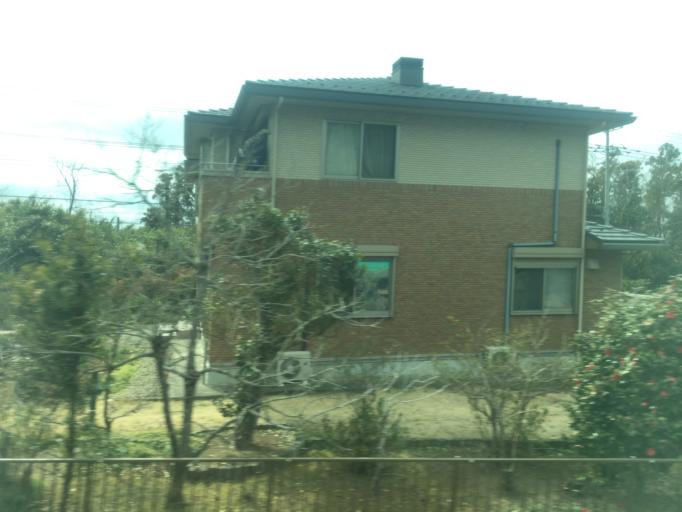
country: JP
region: Chiba
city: Narita
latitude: 35.8133
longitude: 140.2715
